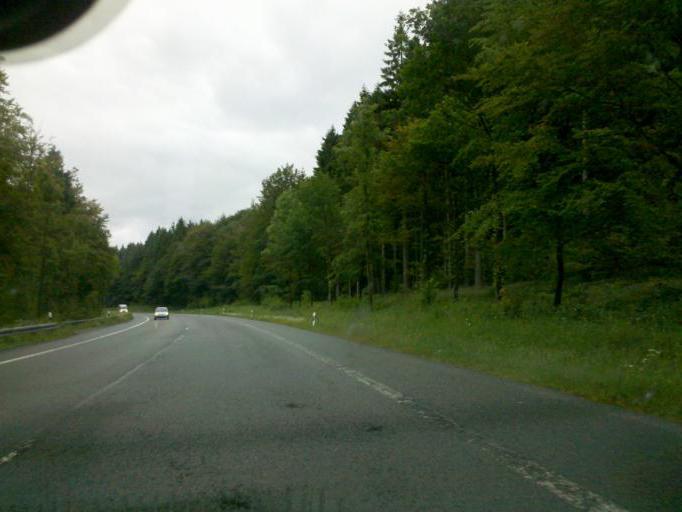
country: DE
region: North Rhine-Westphalia
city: Warstein
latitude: 51.4052
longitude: 8.3170
